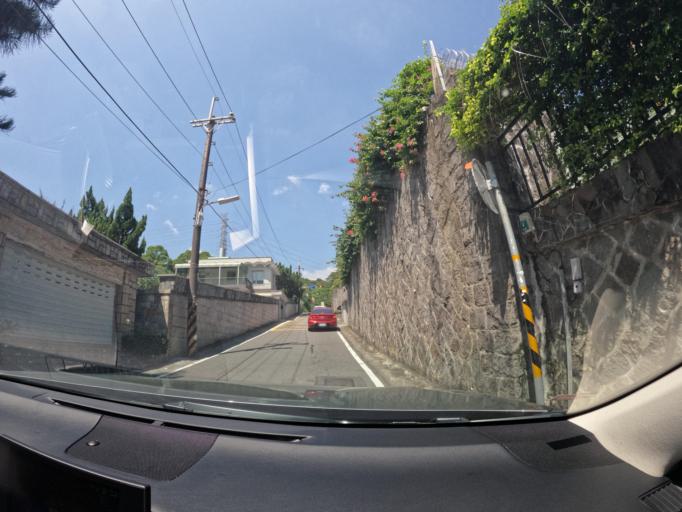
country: TW
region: Taipei
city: Taipei
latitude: 25.1207
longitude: 121.5420
